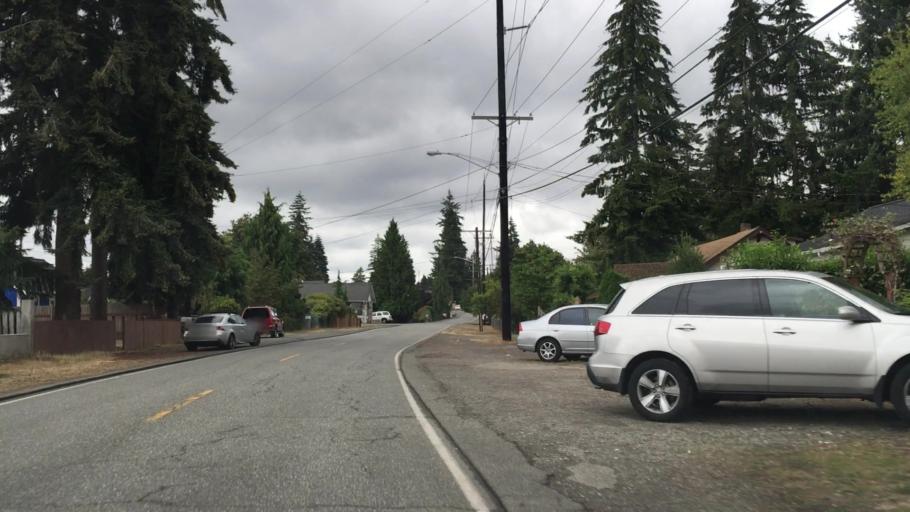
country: US
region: Washington
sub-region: Snohomish County
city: Everett
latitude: 47.9463
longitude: -122.2028
